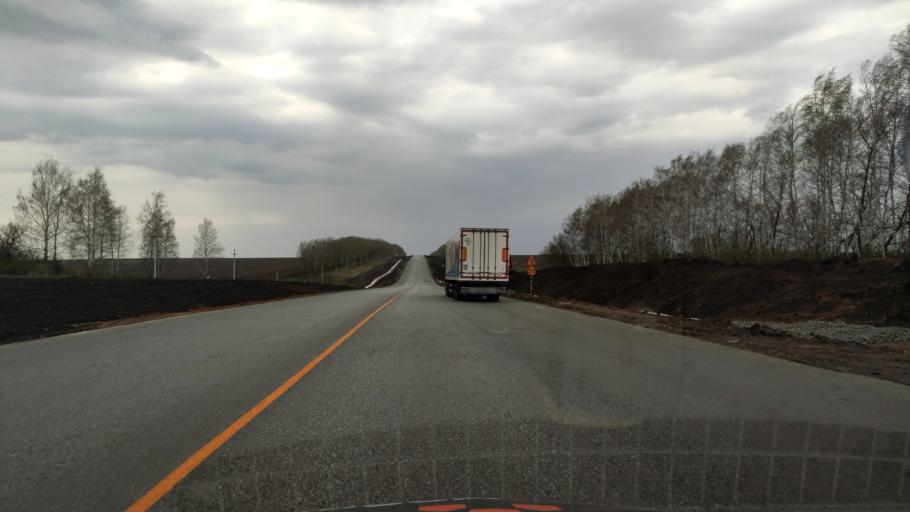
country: RU
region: Kursk
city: Gorshechnoye
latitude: 51.5484
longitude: 38.1087
